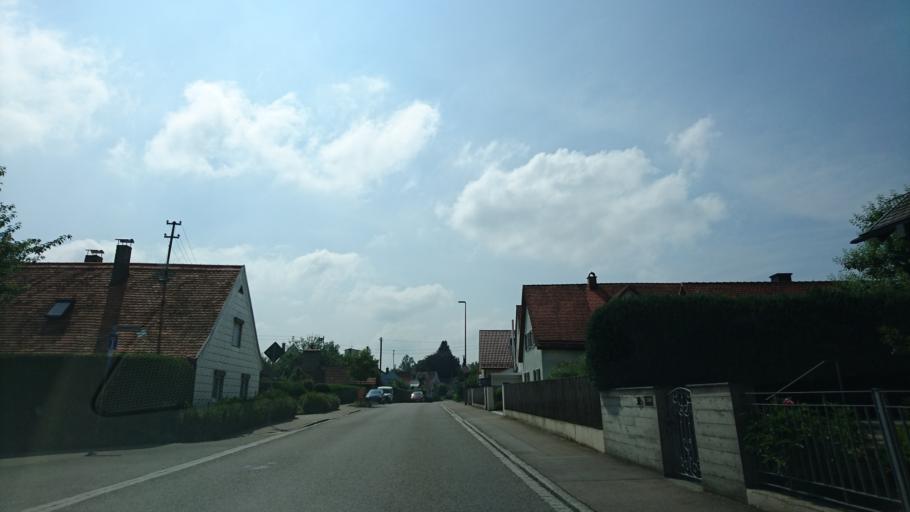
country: DE
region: Bavaria
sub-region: Swabia
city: Stadtbergen
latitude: 48.3649
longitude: 10.8141
